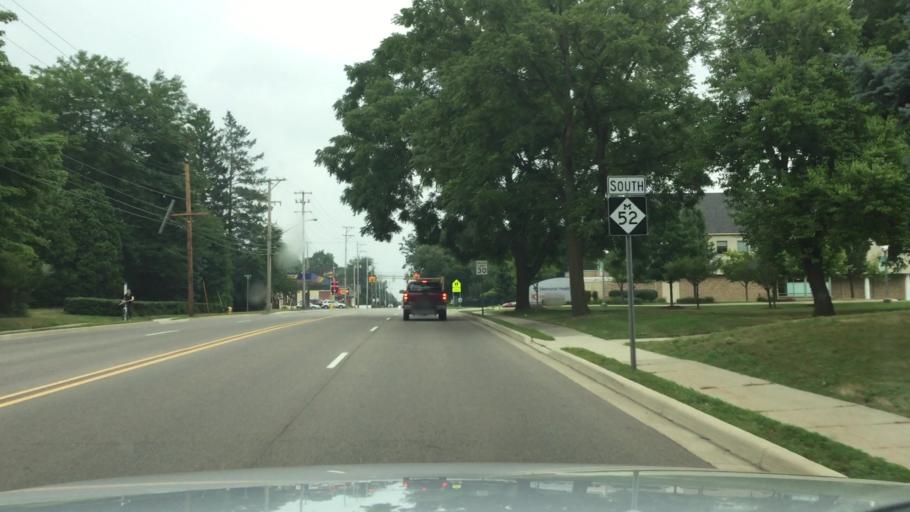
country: US
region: Michigan
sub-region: Shiawassee County
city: Owosso
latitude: 43.0066
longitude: -84.1769
